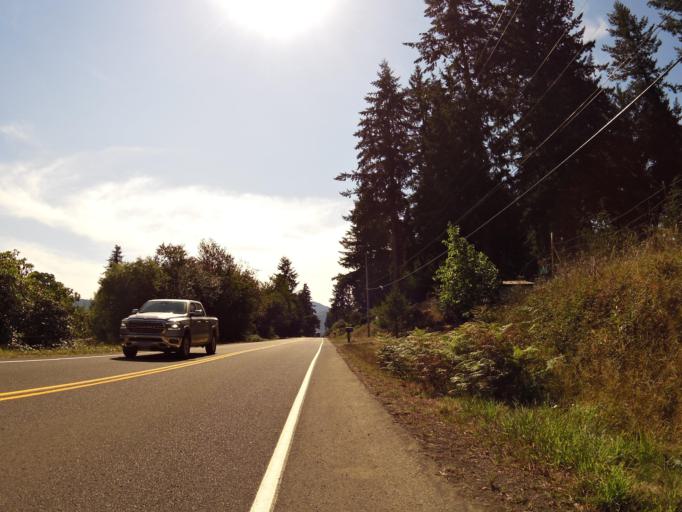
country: US
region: Washington
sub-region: Wahkiakum County
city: Cathlamet
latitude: 46.1779
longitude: -123.5831
